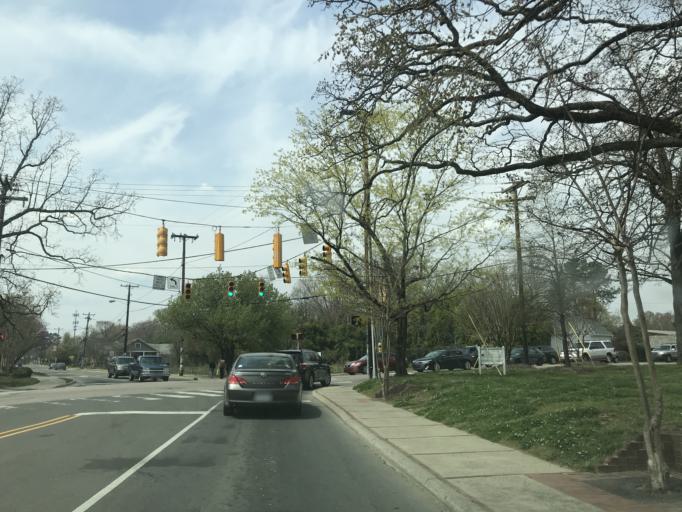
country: US
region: North Carolina
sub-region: Orange County
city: Carrboro
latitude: 35.9110
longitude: -79.0719
